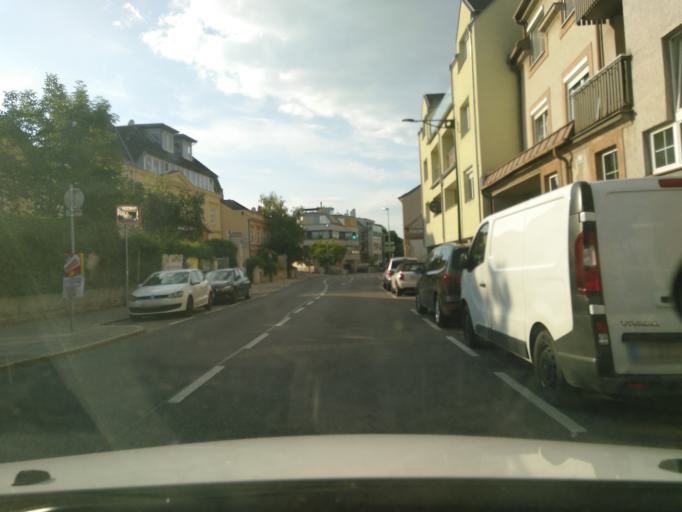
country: AT
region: Lower Austria
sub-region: Politischer Bezirk Modling
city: Modling
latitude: 48.0884
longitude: 16.2838
